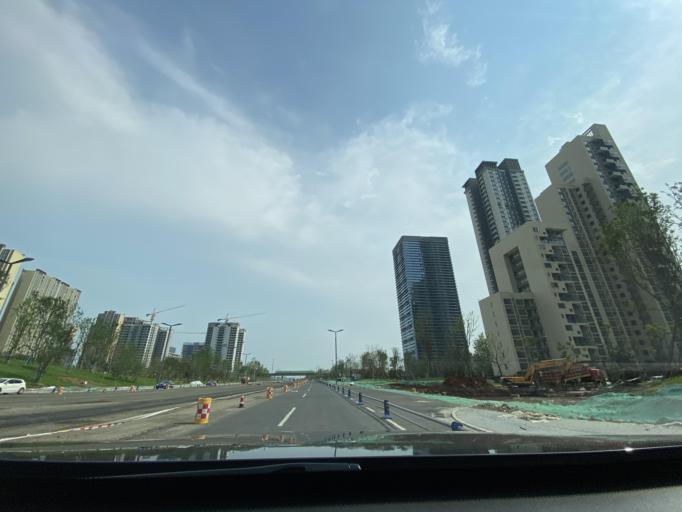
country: CN
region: Sichuan
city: Longquan
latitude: 30.4180
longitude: 104.1013
